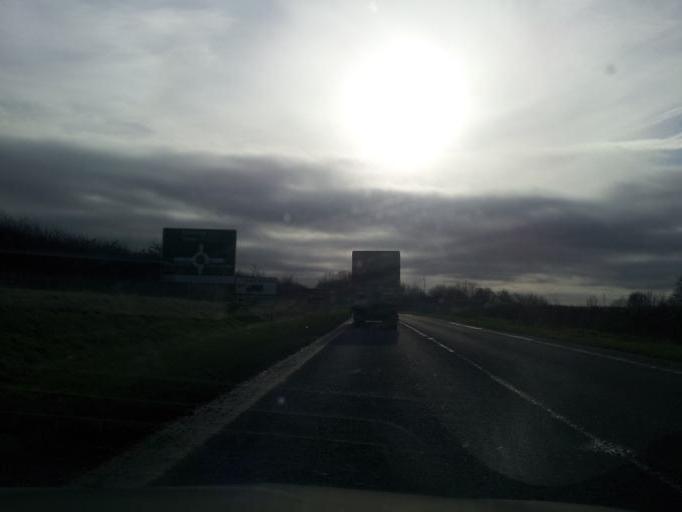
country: GB
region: England
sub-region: District of Rutland
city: Ketton
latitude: 52.6016
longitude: -0.5360
